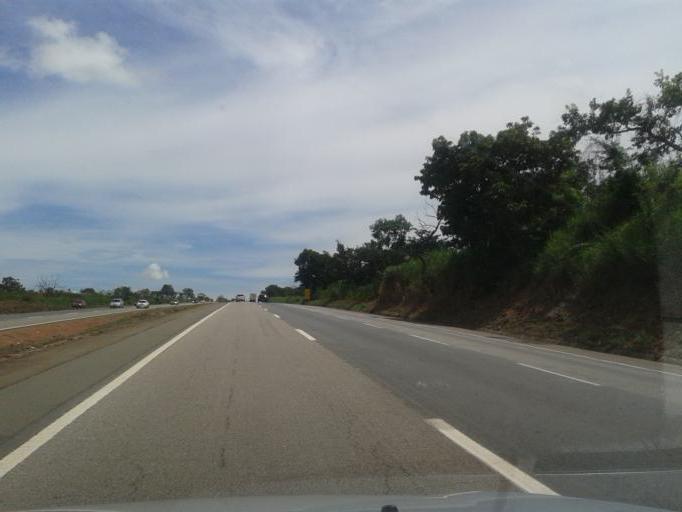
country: BR
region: Goias
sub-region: Hidrolandia
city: Hidrolandia
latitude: -17.0682
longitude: -49.2244
